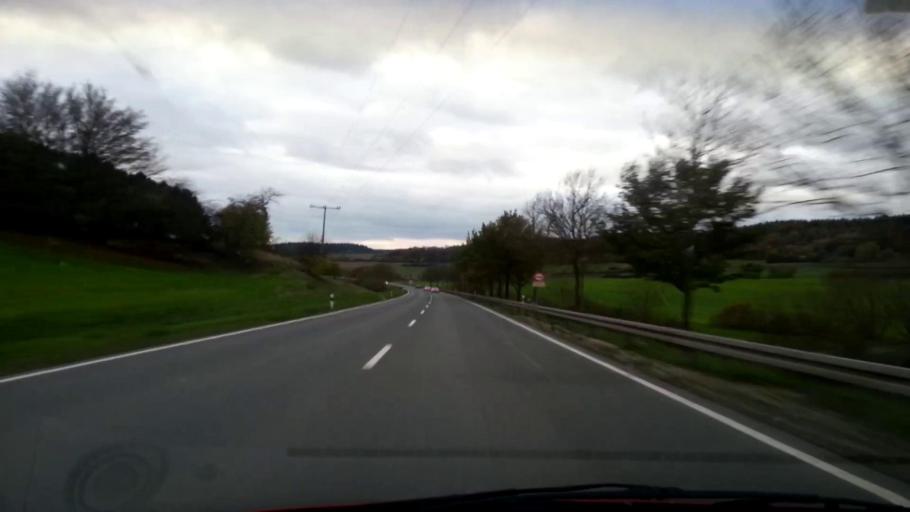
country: DE
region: Bavaria
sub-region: Upper Franconia
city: Kueps Oberfranken
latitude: 50.2118
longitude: 11.2463
